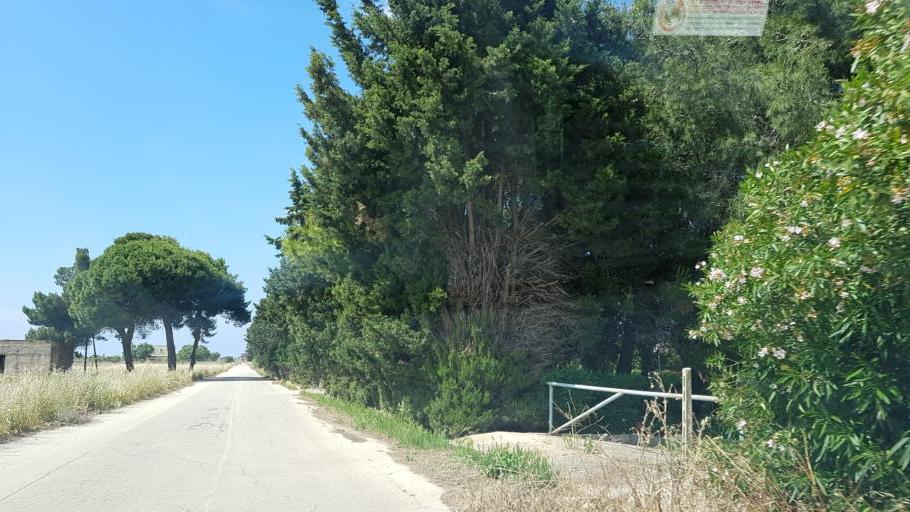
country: IT
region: Apulia
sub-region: Provincia di Brindisi
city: Brindisi
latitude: 40.6543
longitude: 17.8532
